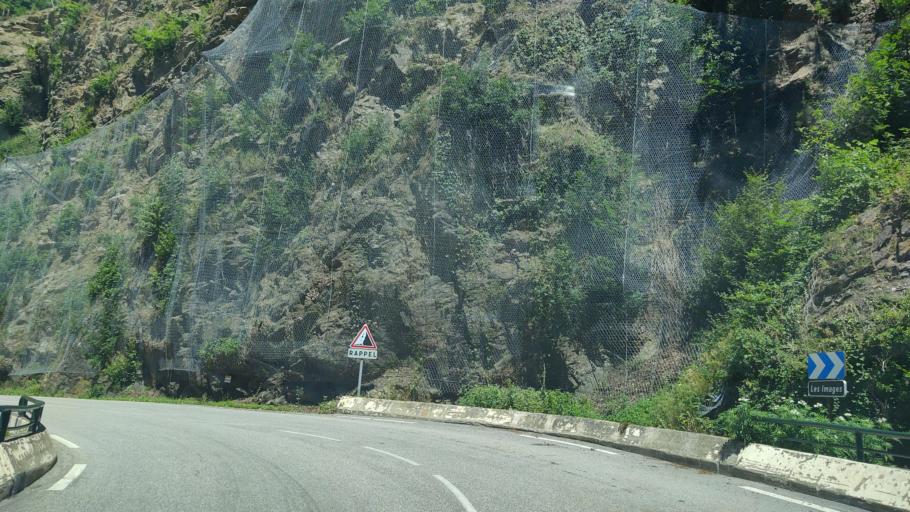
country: FR
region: Rhone-Alpes
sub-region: Departement de la Savoie
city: Ugine
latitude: 45.7539
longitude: 6.4590
